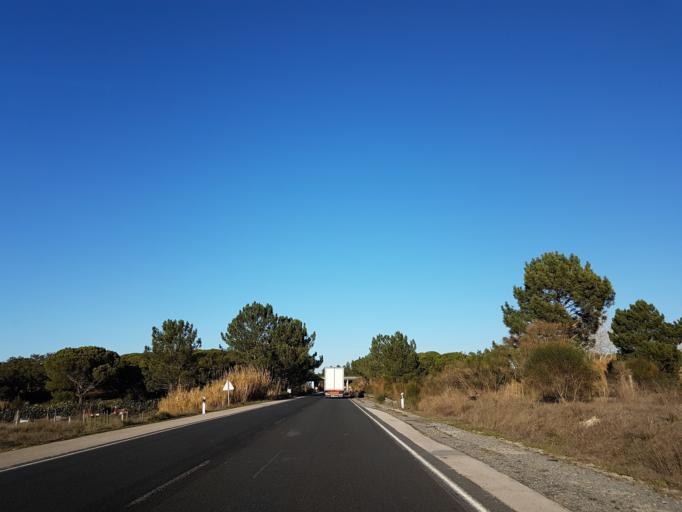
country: PT
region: Setubal
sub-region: Alcacer do Sal
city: Alcacer do Sal
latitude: 38.4007
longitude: -8.5177
